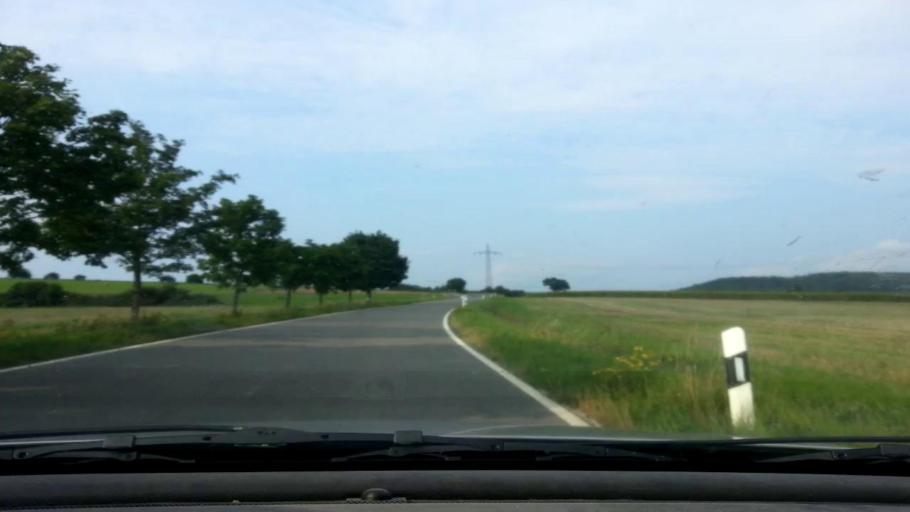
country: DE
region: Bavaria
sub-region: Upper Franconia
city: Litzendorf
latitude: 49.8731
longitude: 11.0036
